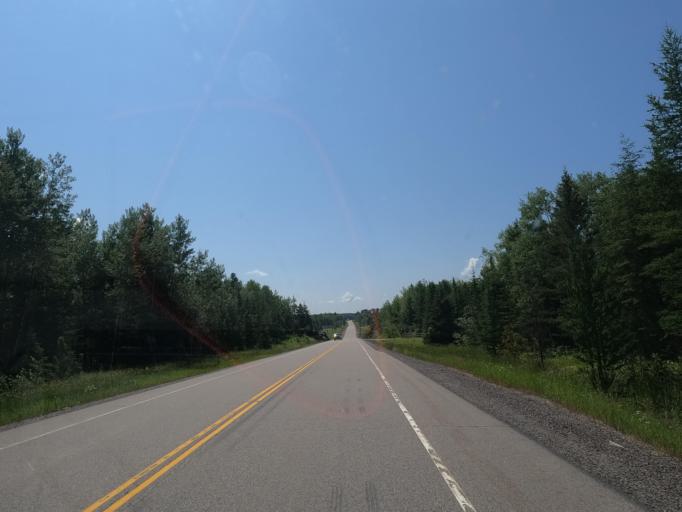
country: CA
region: Ontario
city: Dryden
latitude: 49.8834
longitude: -93.3591
